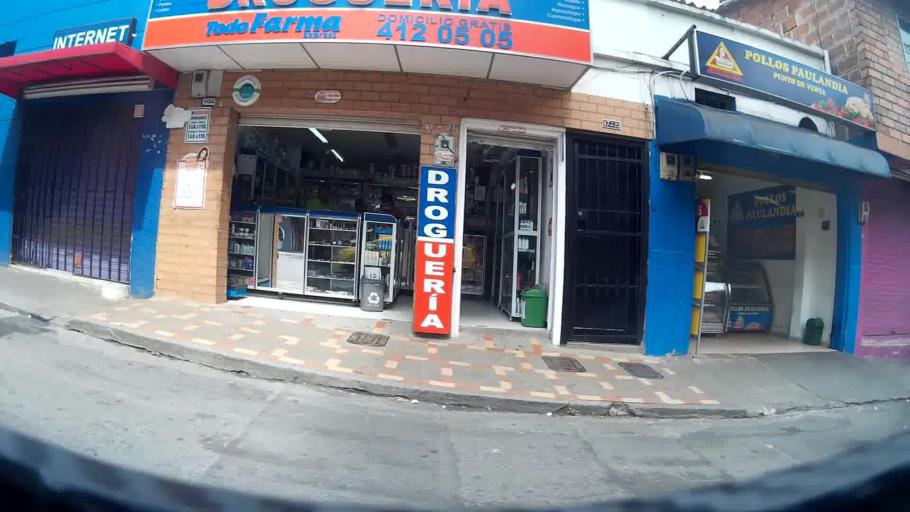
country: CO
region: Antioquia
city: Medellin
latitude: 6.2576
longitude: -75.6035
